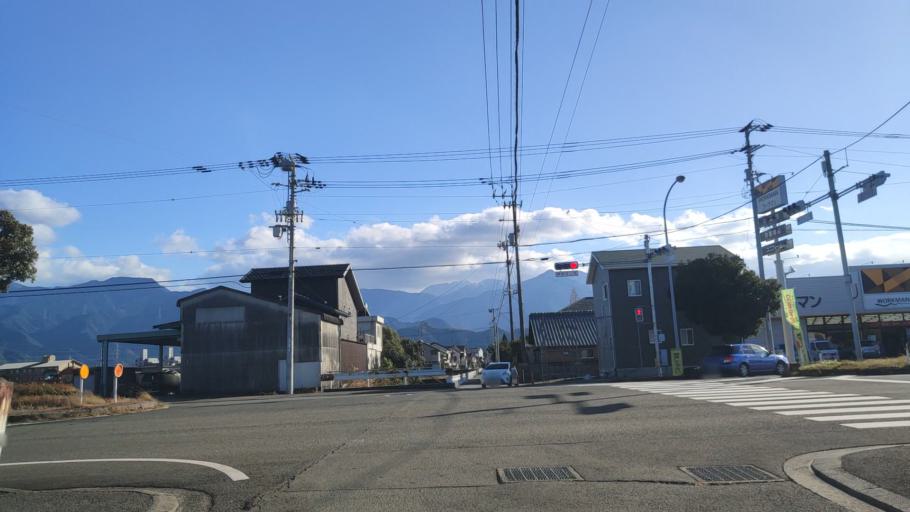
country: JP
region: Ehime
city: Saijo
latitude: 33.9198
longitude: 133.1623
